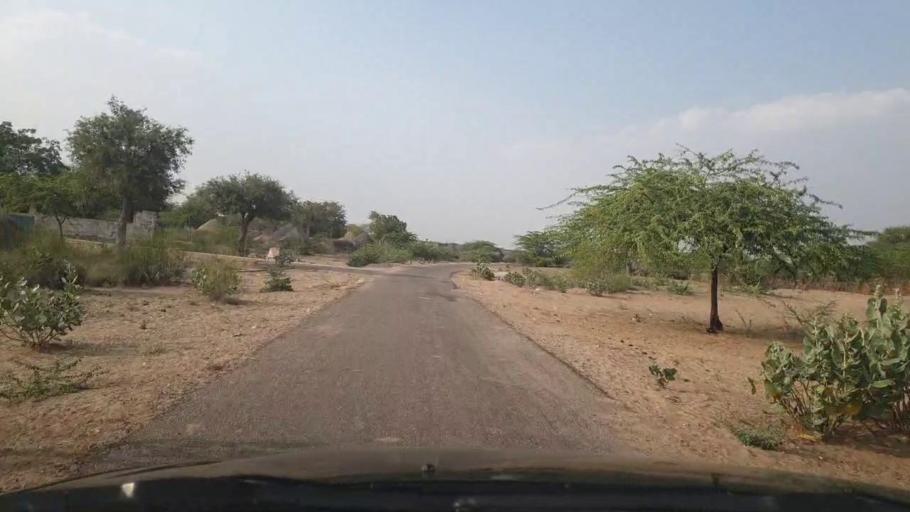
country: PK
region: Sindh
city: Islamkot
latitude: 25.0674
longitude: 70.5657
